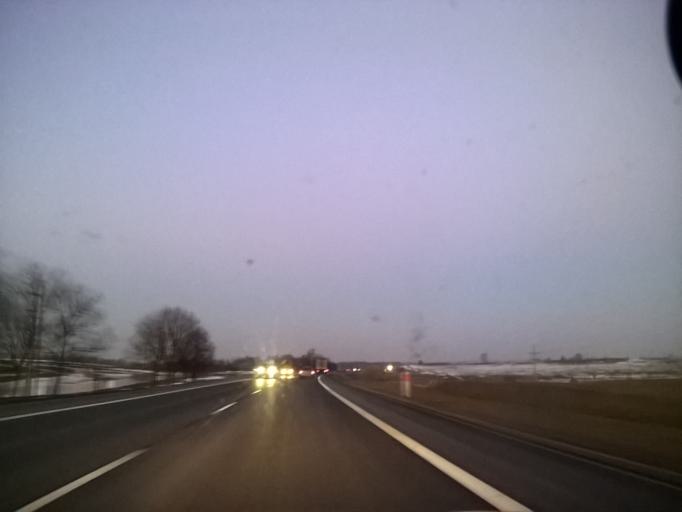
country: PL
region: Warmian-Masurian Voivodeship
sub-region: Powiat olsztynski
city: Biskupiec
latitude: 53.8393
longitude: 20.9320
